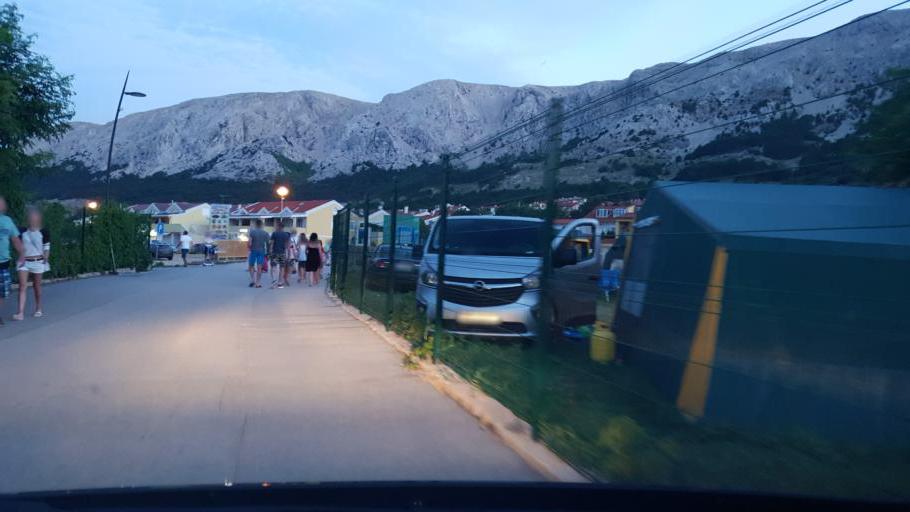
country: HR
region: Primorsko-Goranska
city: Punat
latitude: 44.9639
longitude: 14.7461
